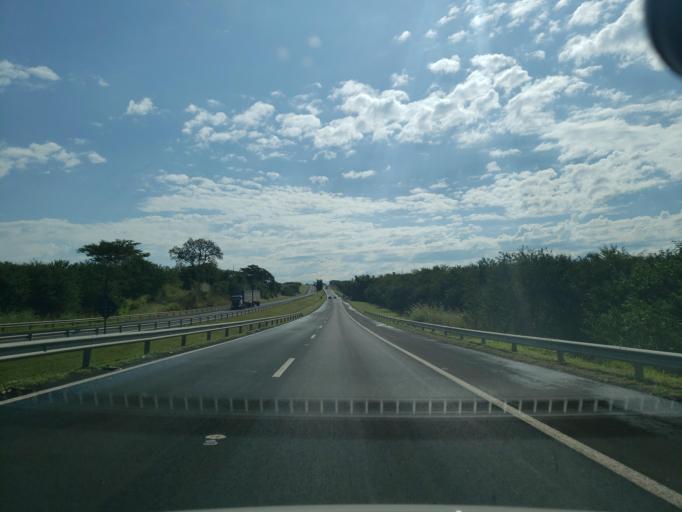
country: BR
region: Sao Paulo
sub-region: Pirajui
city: Pirajui
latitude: -22.0291
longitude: -49.4040
